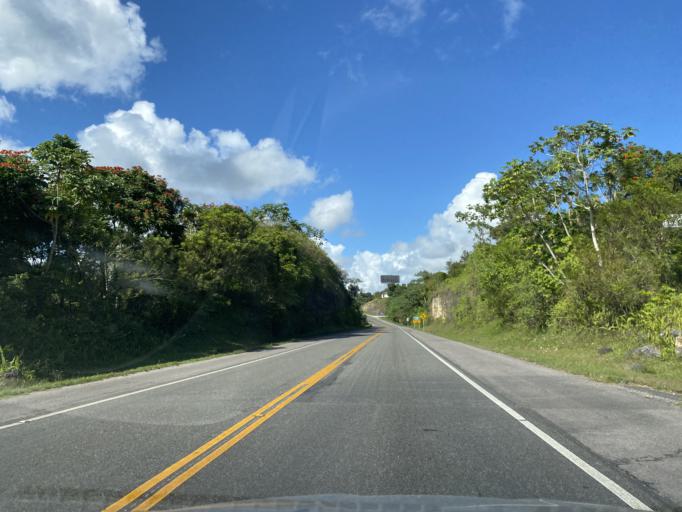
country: DO
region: Monte Plata
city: Majagual
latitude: 19.0389
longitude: -69.8283
